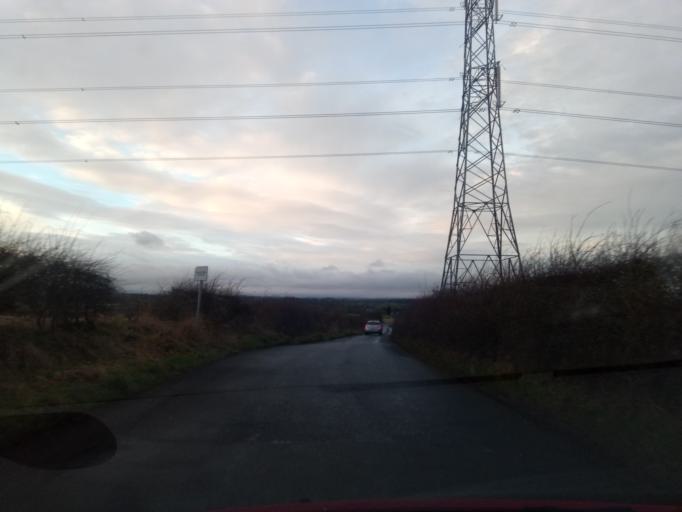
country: GB
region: England
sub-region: Northumberland
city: Ponteland
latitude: 55.0789
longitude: -1.7373
